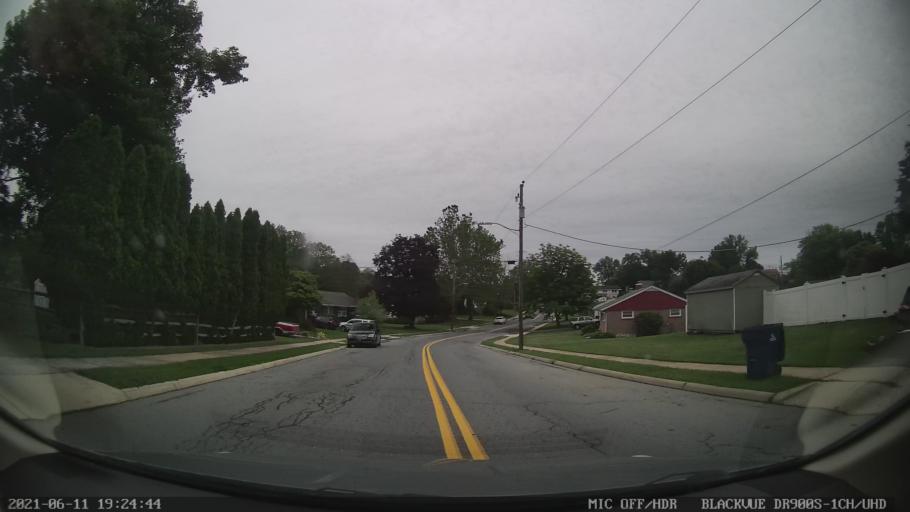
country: US
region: Pennsylvania
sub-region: Berks County
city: Sinking Spring
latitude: 40.3294
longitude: -76.0104
